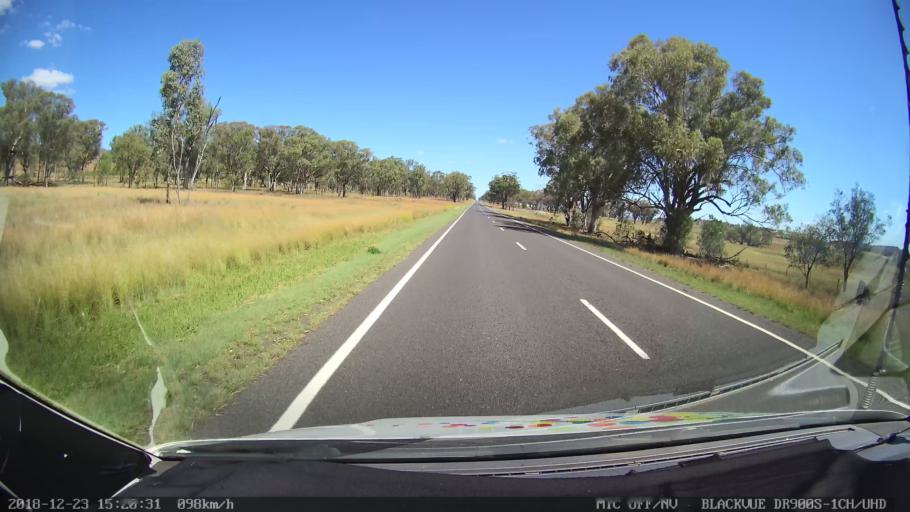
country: AU
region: New South Wales
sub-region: Tamworth Municipality
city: Manilla
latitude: -30.8438
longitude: 150.7903
